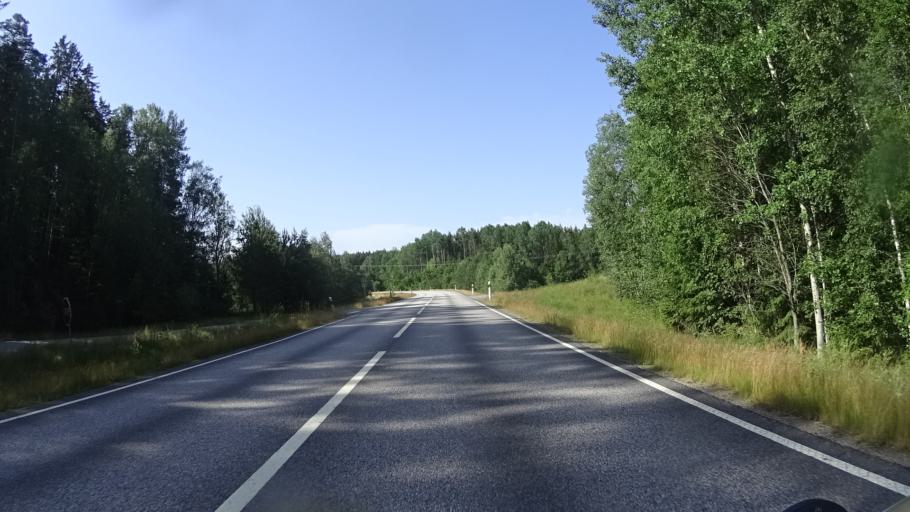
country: SE
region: Kalmar
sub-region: Vasterviks Kommun
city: Overum
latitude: 58.0569
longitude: 16.2042
